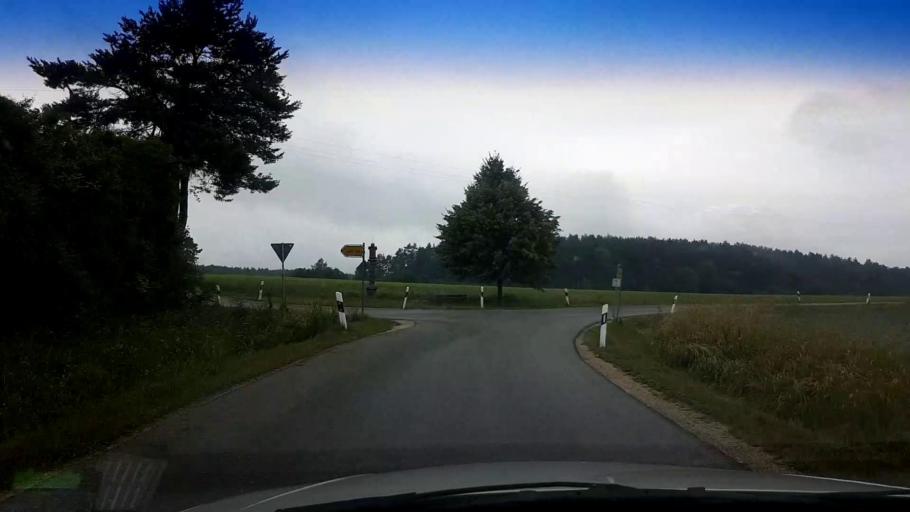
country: DE
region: Bavaria
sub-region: Upper Franconia
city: Altendorf
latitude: 50.0581
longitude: 11.1488
